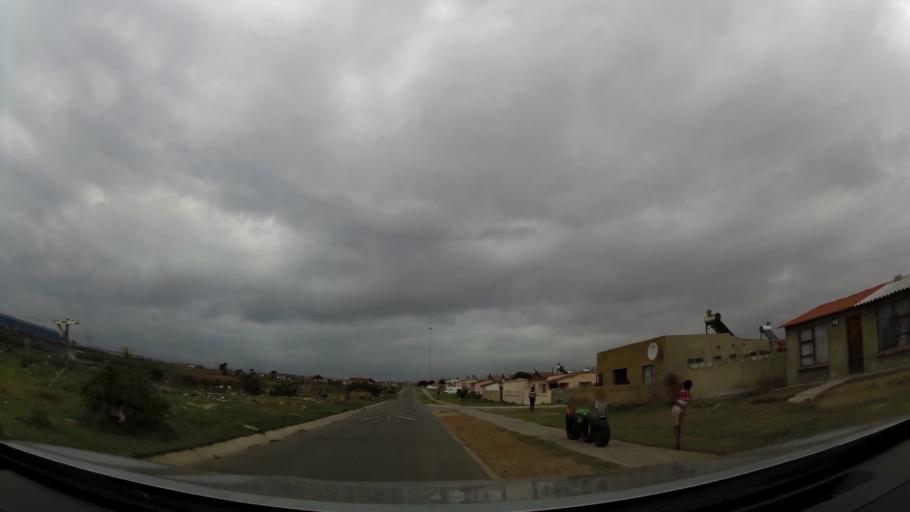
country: ZA
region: Eastern Cape
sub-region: Nelson Mandela Bay Metropolitan Municipality
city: Port Elizabeth
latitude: -33.8782
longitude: 25.6010
